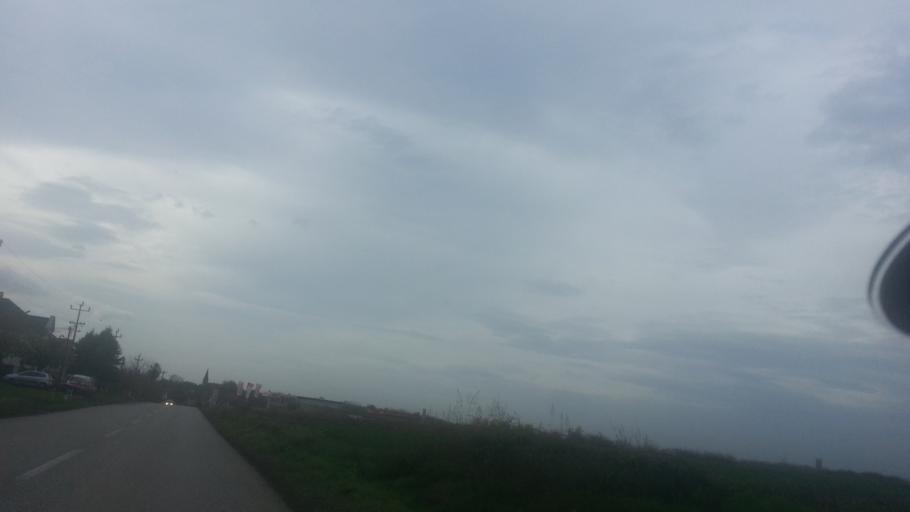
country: RS
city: Putinci
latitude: 44.9913
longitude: 19.9861
